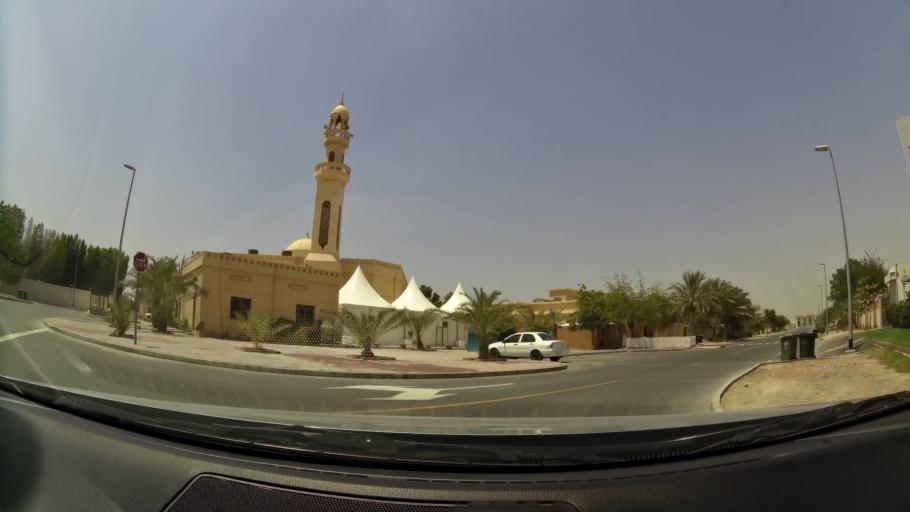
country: AE
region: Dubai
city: Dubai
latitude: 25.0931
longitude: 55.2080
